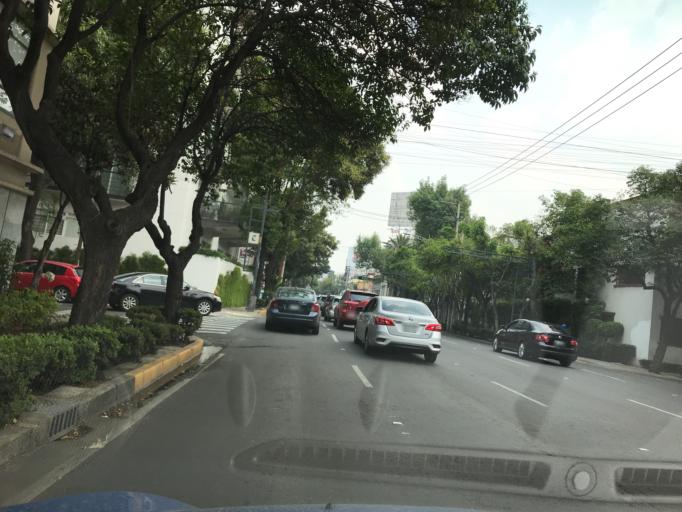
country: MX
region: Mexico City
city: Colonia del Valle
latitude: 19.3832
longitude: -99.1676
